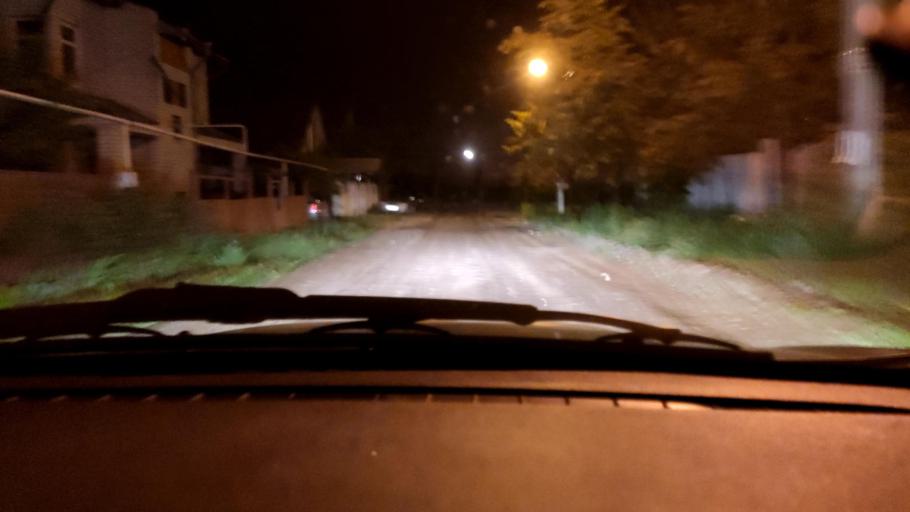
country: RU
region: Voronezj
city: Pridonskoy
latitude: 51.6822
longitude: 39.0640
